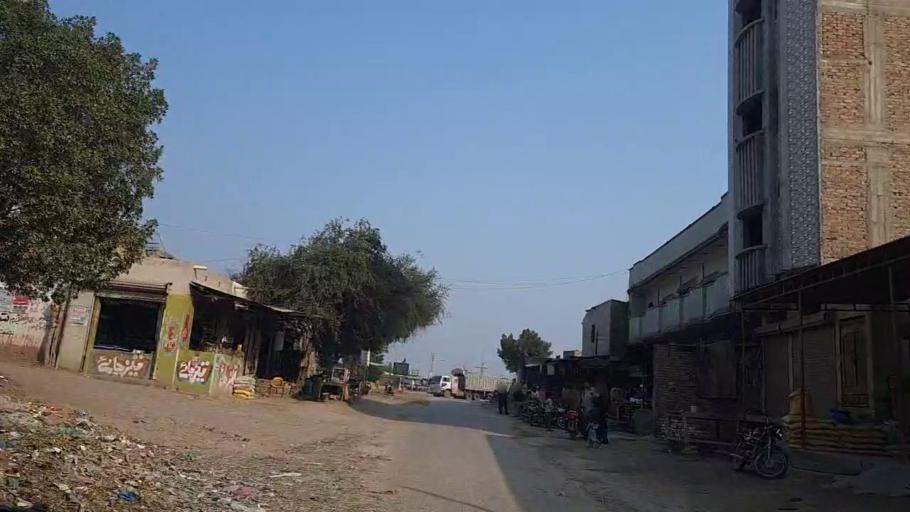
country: PK
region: Sindh
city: Sakrand
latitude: 26.1383
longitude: 68.2589
